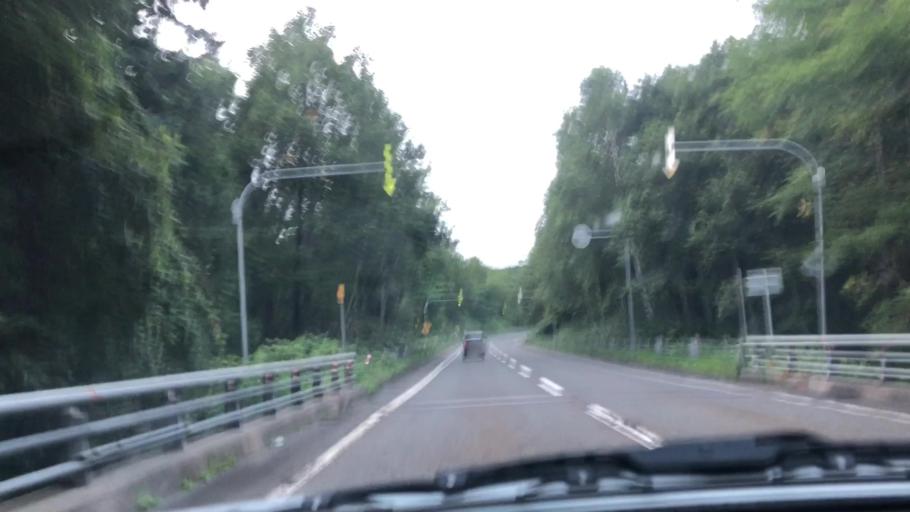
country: JP
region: Hokkaido
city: Iwamizawa
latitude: 42.9042
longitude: 142.1273
